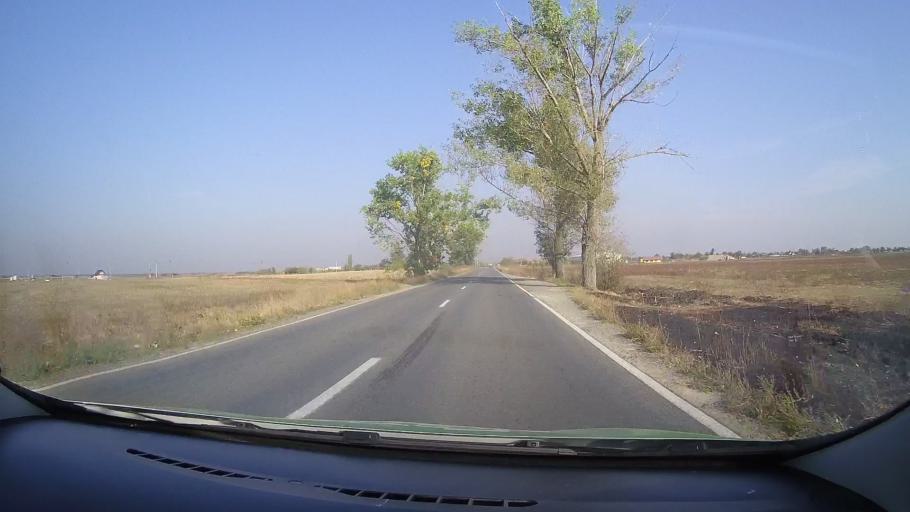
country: RO
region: Arad
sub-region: Comuna Pilu
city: Pilu
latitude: 46.5659
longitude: 21.3449
